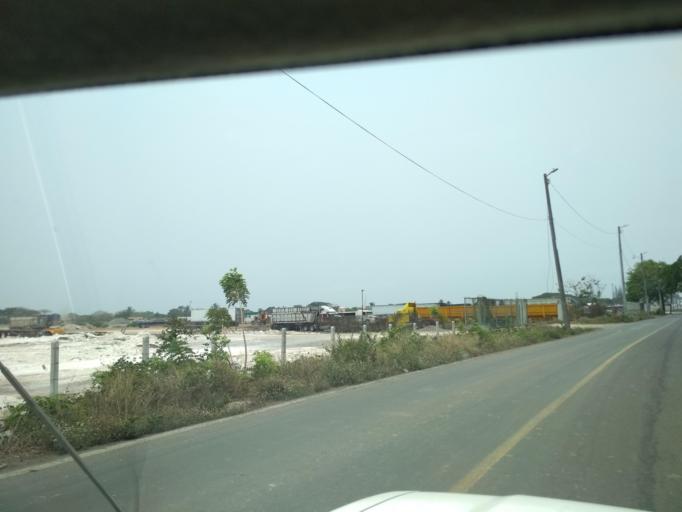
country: MX
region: Veracruz
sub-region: Veracruz
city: Delfino Victoria (Santa Fe)
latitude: 19.2078
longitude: -96.2640
